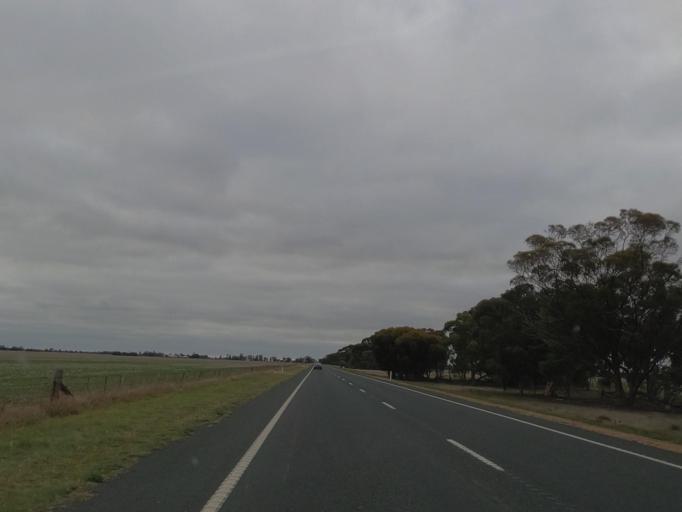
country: AU
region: Victoria
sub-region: Greater Bendigo
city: Long Gully
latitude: -36.2655
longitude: 143.9655
